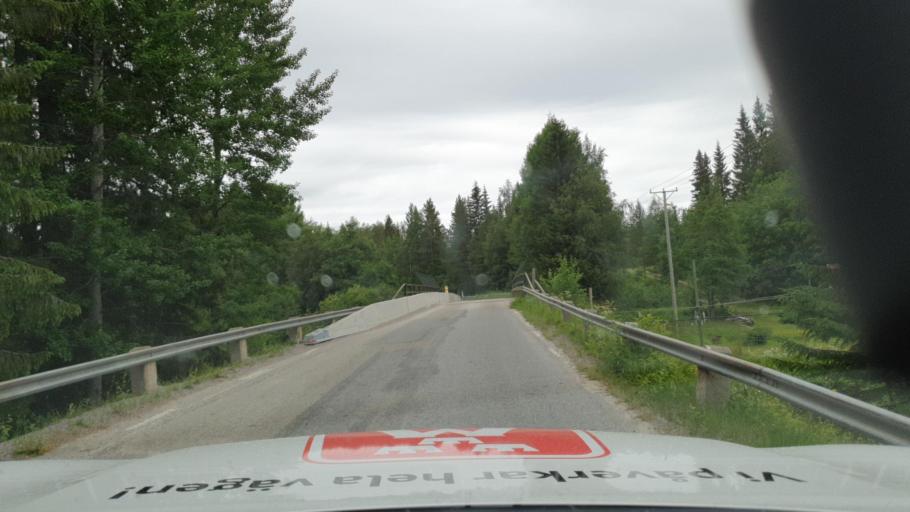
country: SE
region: Vaesterbotten
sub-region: Nordmalings Kommun
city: Nordmaling
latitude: 63.7685
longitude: 19.4256
